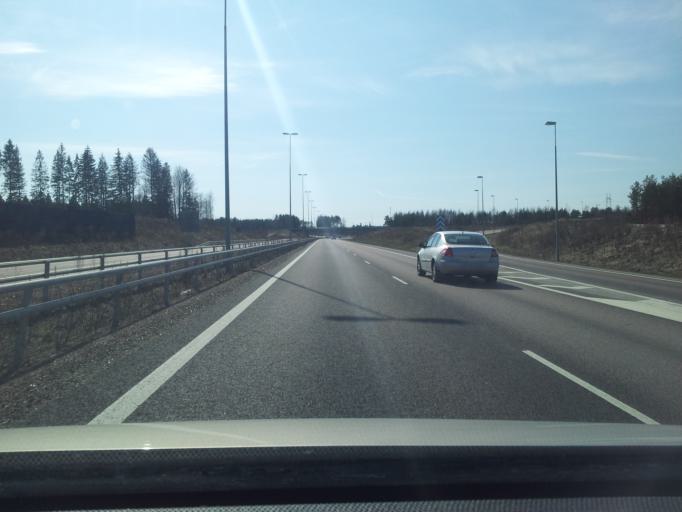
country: FI
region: Kymenlaakso
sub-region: Kotka-Hamina
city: Hamina
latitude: 60.5774
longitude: 27.1388
